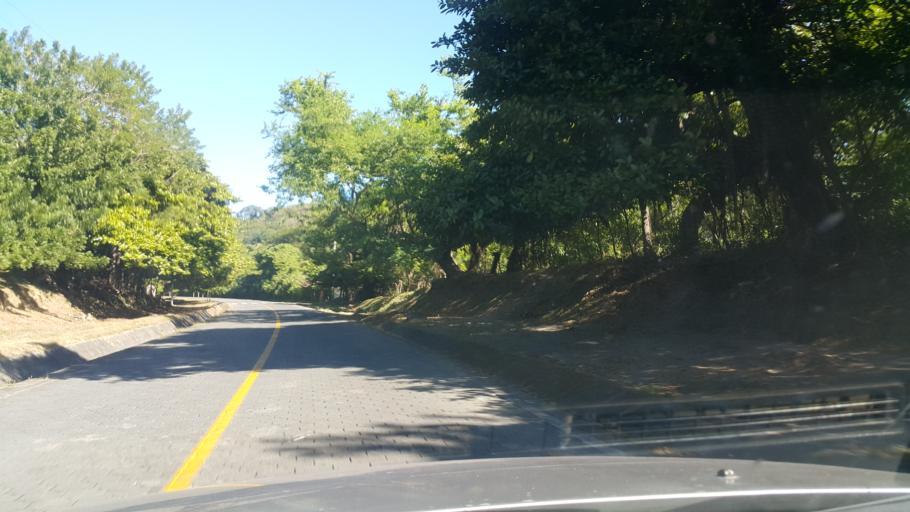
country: NI
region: Rivas
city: Moyogalpa
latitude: 11.4860
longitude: -85.6366
